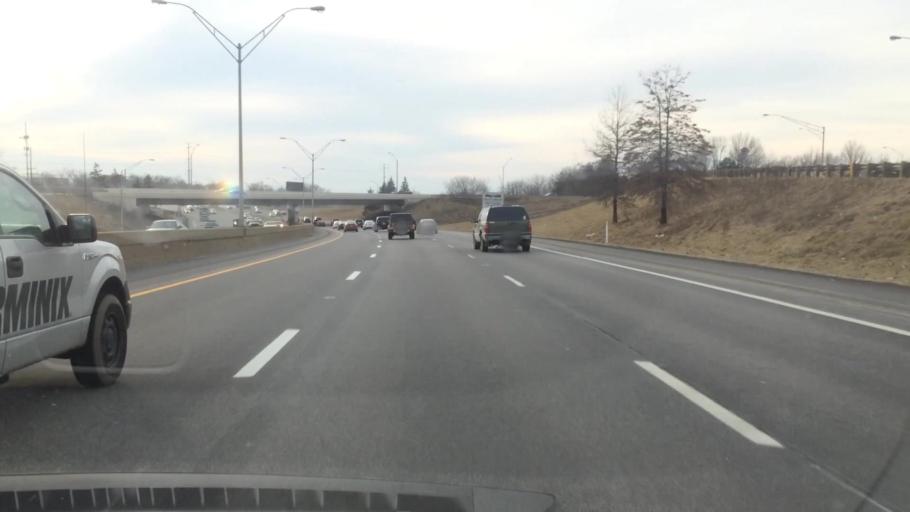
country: US
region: Ohio
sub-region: Cuyahoga County
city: Maple Heights
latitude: 41.4240
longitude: -81.5769
